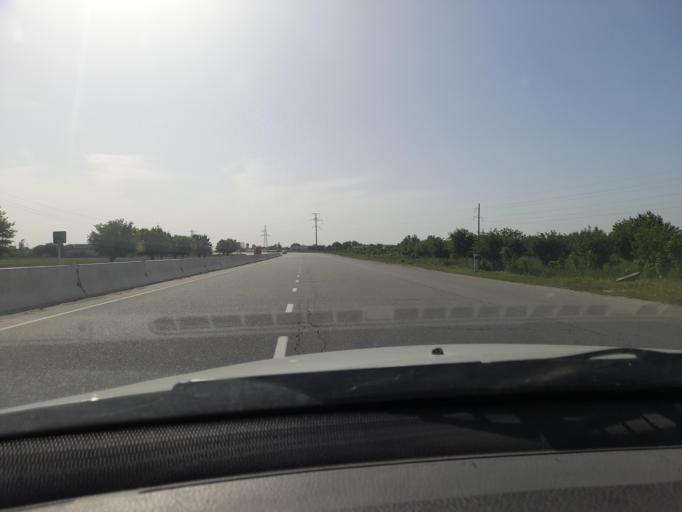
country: UZ
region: Samarqand
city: Ishtixon
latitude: 39.9583
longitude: 66.4650
